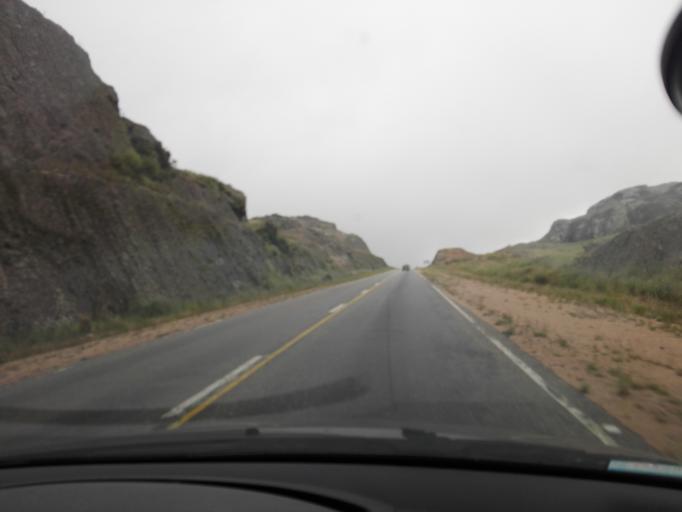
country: AR
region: Cordoba
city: Cuesta Blanca
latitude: -31.6164
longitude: -64.7418
